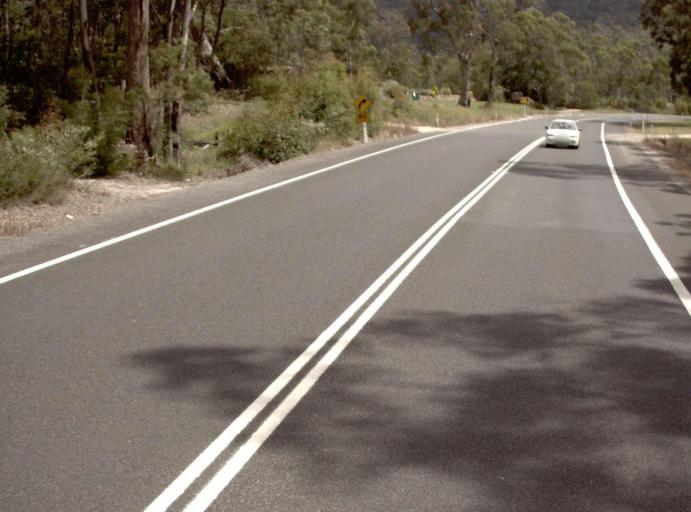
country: AU
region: New South Wales
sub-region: Bega Valley
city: Eden
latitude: -37.4805
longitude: 149.5824
